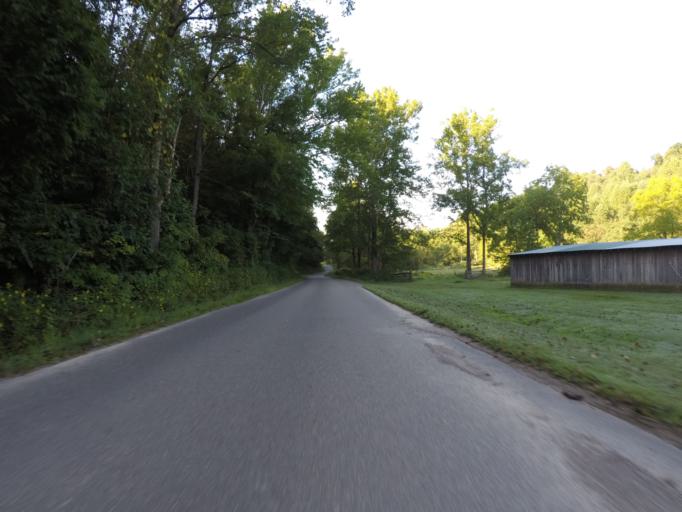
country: US
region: Ohio
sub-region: Lawrence County
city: Coal Grove
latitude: 38.5577
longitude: -82.5529
